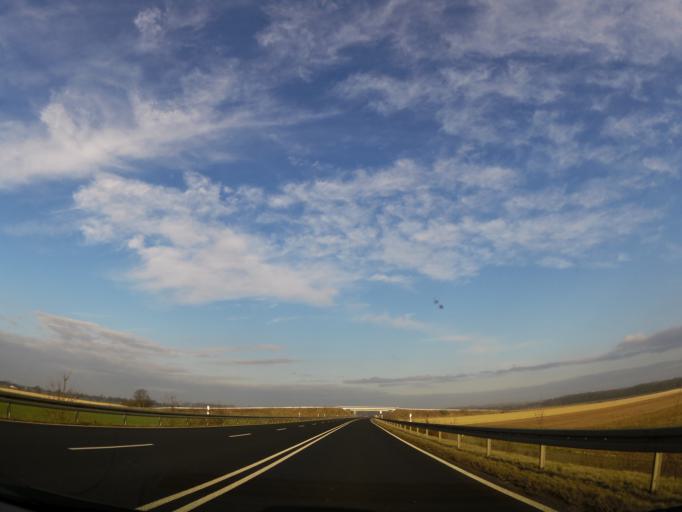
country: DE
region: North Rhine-Westphalia
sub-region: Regierungsbezirk Koln
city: Selfkant
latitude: 51.0254
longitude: 5.9003
